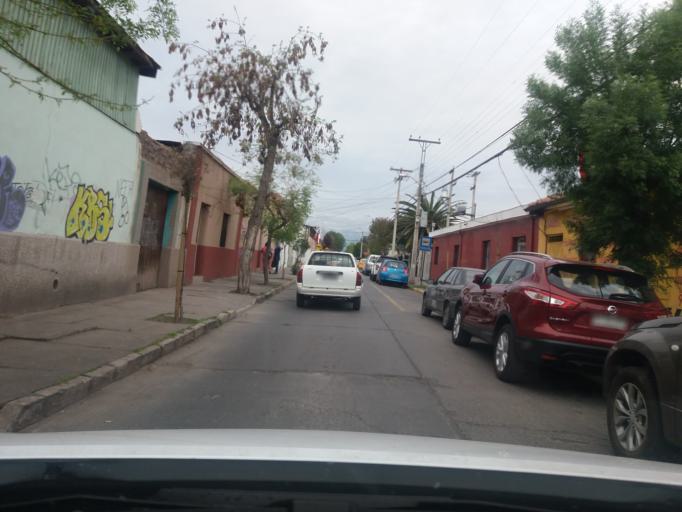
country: CL
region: Valparaiso
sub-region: Provincia de San Felipe
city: San Felipe
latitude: -32.7537
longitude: -70.7251
